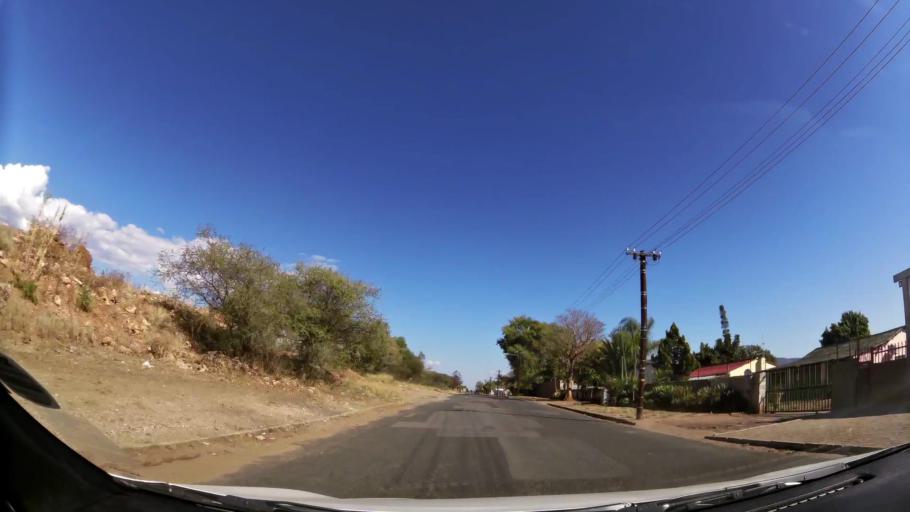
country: ZA
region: Limpopo
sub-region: Waterberg District Municipality
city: Mokopane
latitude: -24.1758
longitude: 29.0180
